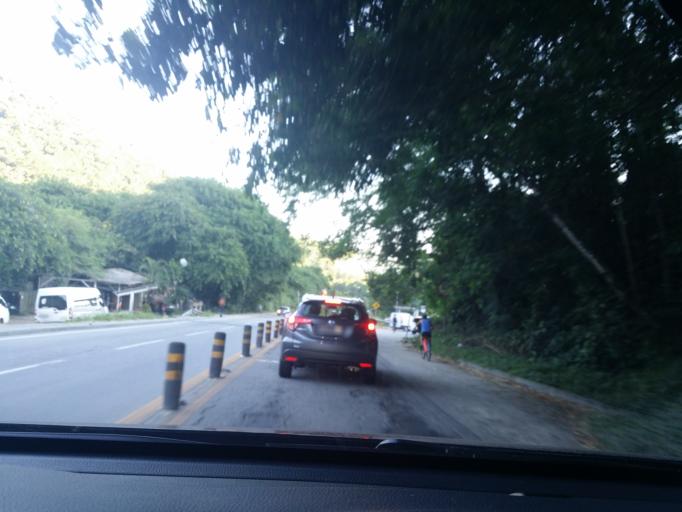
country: BR
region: Sao Paulo
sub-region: Sao Sebastiao
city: Sao Sebastiao
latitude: -23.7502
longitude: -45.7264
